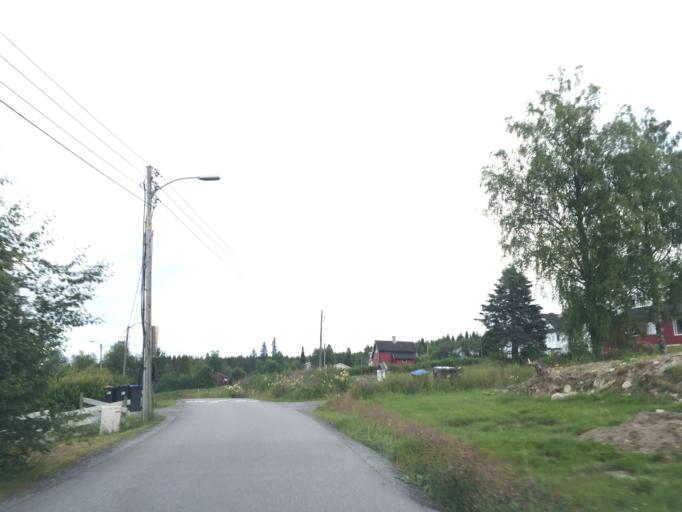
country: NO
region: Hedmark
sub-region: Kongsvinger
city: Kongsvinger
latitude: 60.1808
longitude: 11.9892
